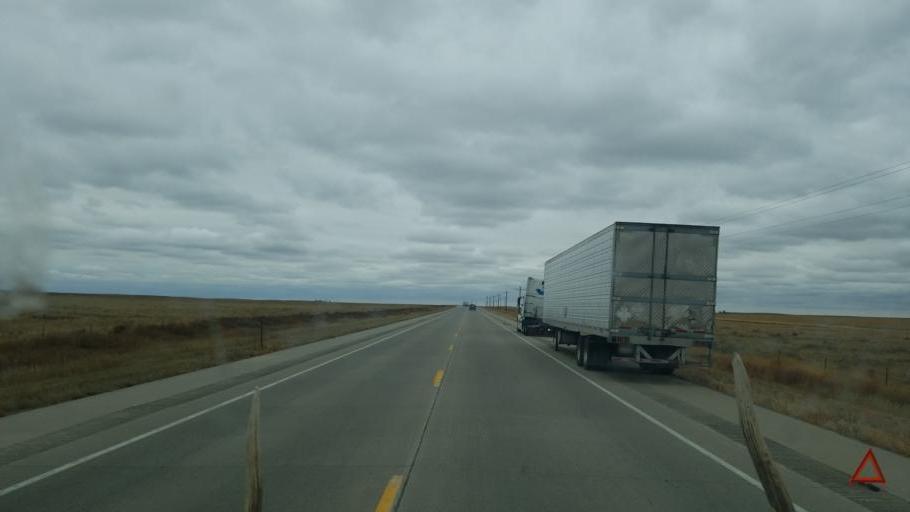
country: US
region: Colorado
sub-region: Kiowa County
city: Eads
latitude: 38.6671
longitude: -102.7858
